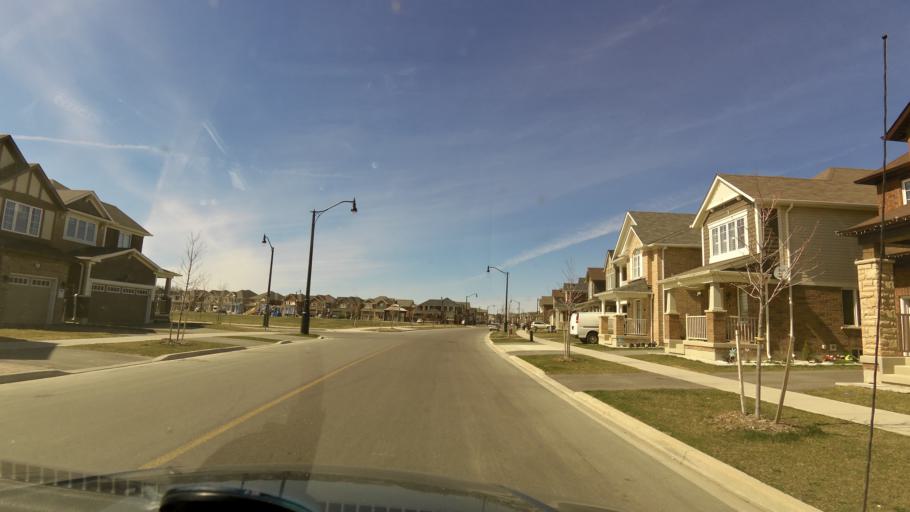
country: CA
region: Ontario
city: Brampton
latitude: 43.6876
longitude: -79.8394
